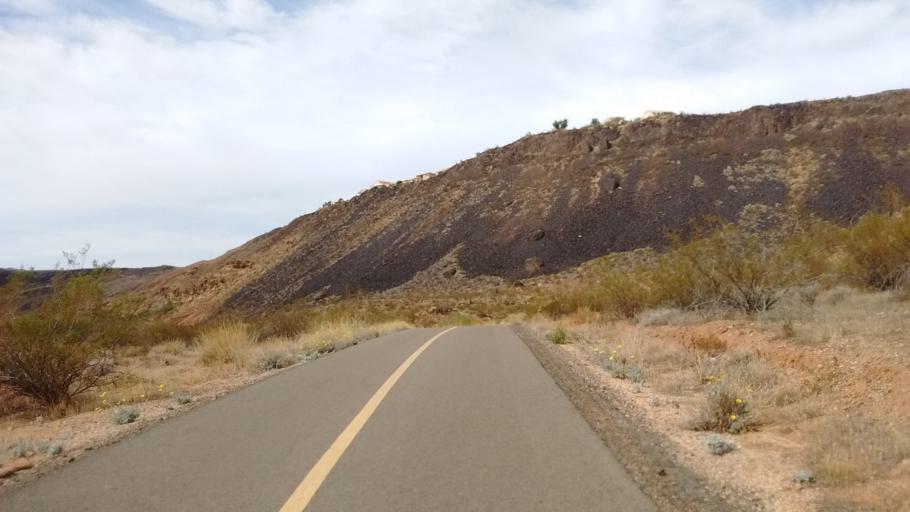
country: US
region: Utah
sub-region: Washington County
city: Washington
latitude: 37.1223
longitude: -113.4842
